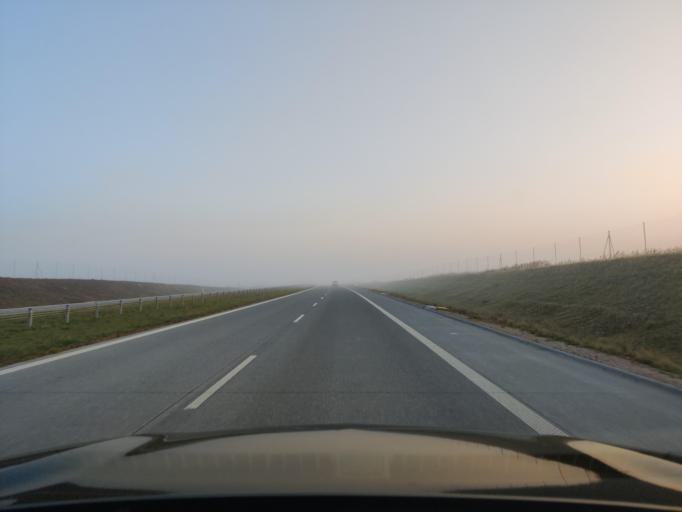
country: PL
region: Masovian Voivodeship
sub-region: Powiat mlawski
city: Strzegowo
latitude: 52.9445
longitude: 20.2972
